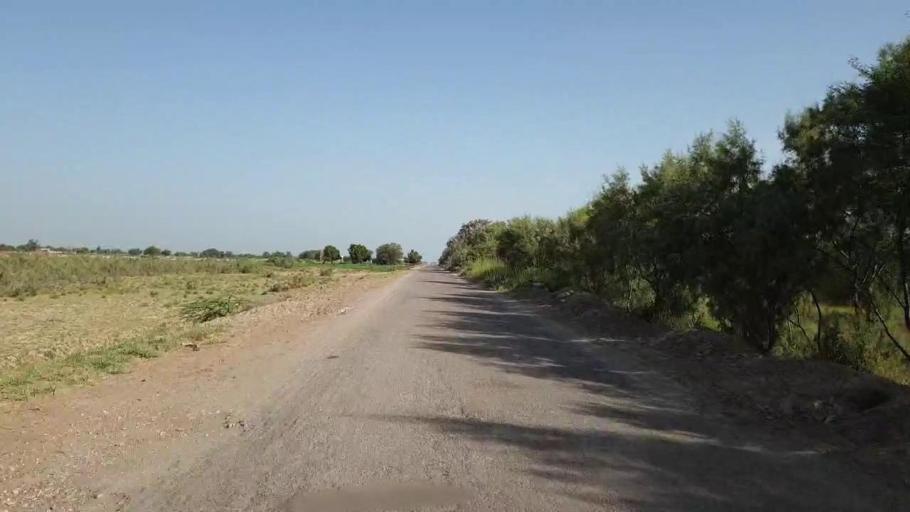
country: PK
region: Sindh
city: Nawabshah
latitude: 26.1573
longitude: 68.4452
